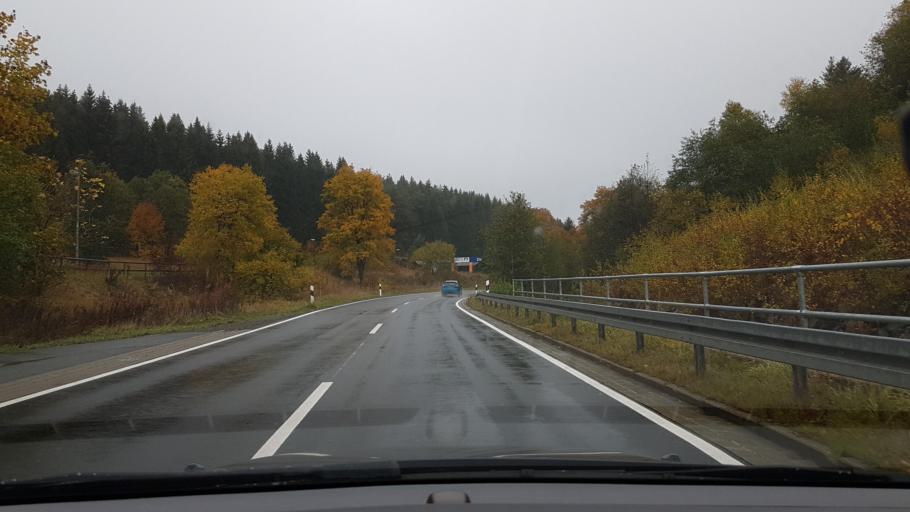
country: DE
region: Lower Saxony
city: Clausthal-Zellerfeld
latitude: 51.8093
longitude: 10.3089
